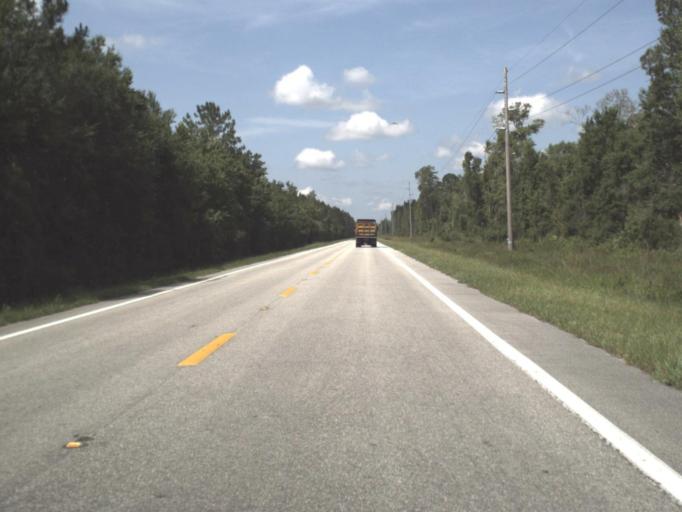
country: US
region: Florida
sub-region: Levy County
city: Bronson
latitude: 29.3936
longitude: -82.6997
